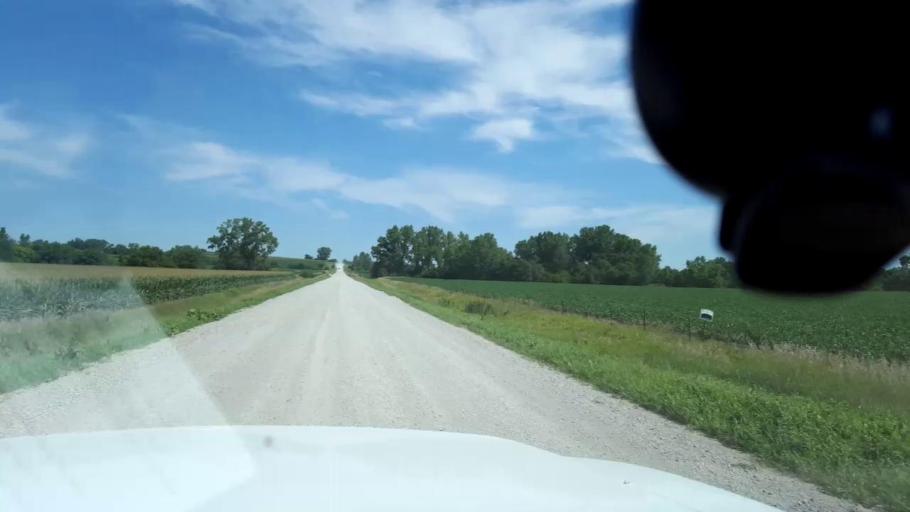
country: US
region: Iowa
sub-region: Pottawattamie County
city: Oakland
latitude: 41.2463
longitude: -95.5371
